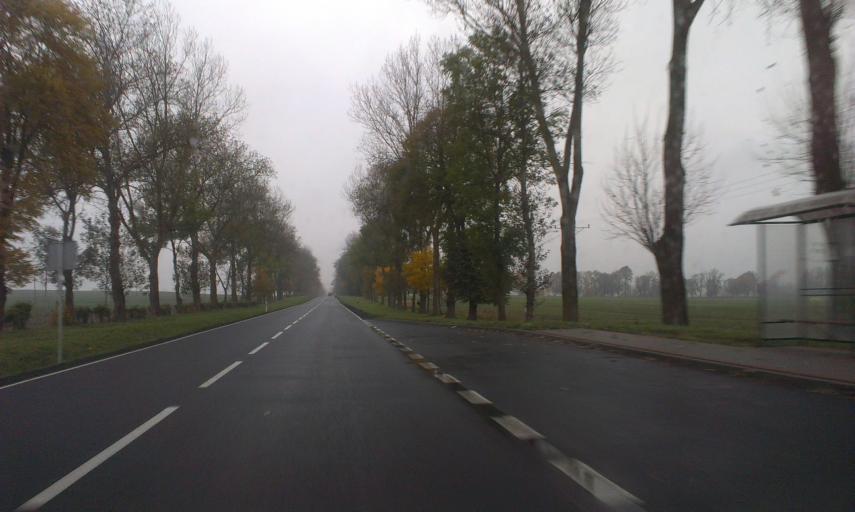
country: PL
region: West Pomeranian Voivodeship
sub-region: Powiat koszalinski
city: Sianow
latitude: 54.1408
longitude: 16.2671
